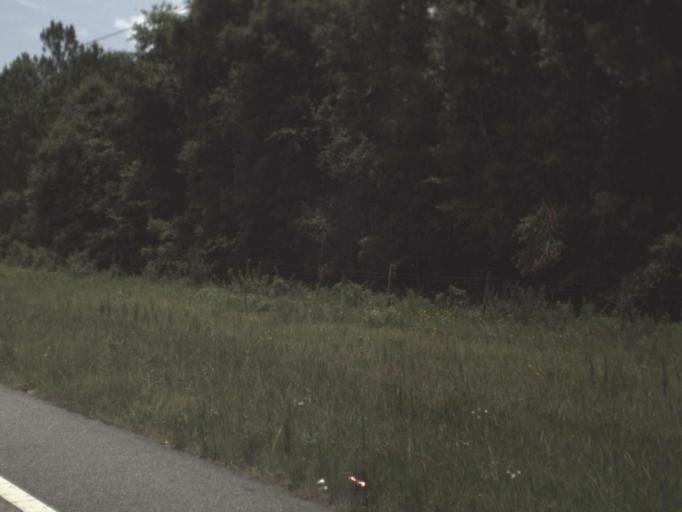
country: US
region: Florida
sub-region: Madison County
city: Madison
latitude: 30.4888
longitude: -83.4724
